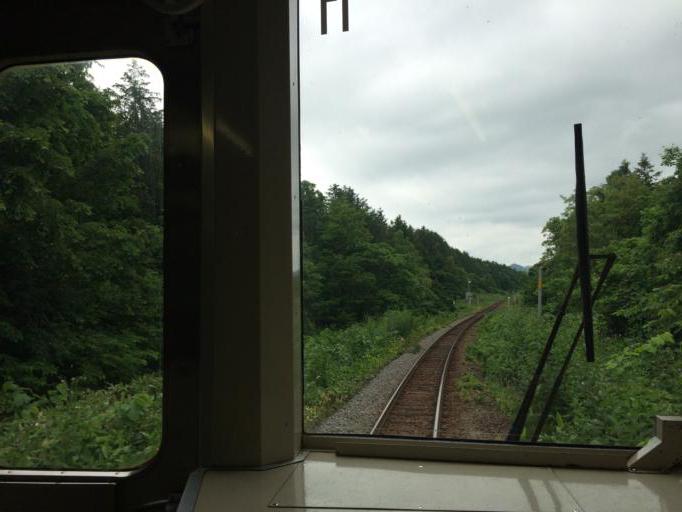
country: JP
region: Hokkaido
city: Yoichi
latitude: 43.0693
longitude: 140.7030
